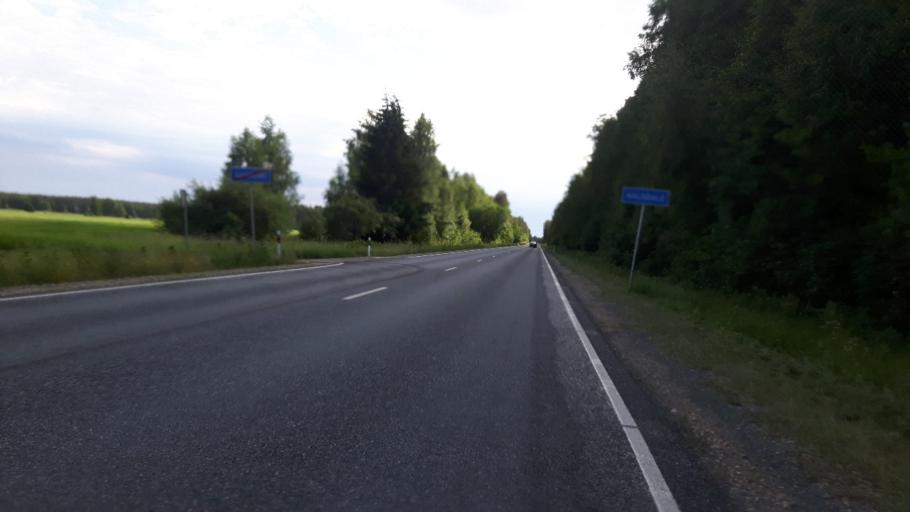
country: LV
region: Riga
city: Jaunciems
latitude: 57.0924
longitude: 24.1827
